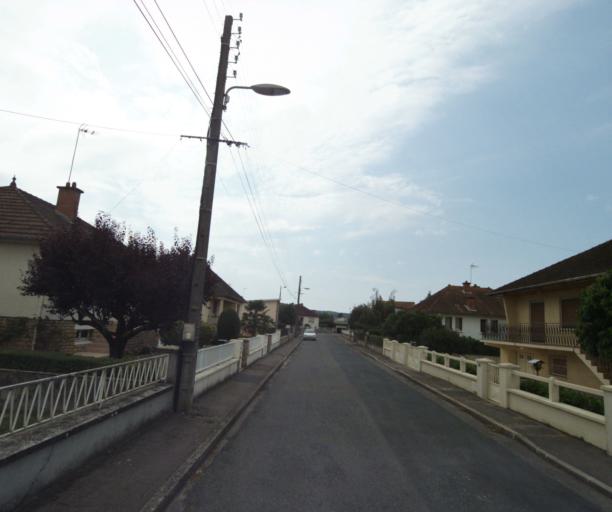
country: FR
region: Bourgogne
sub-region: Departement de Saone-et-Loire
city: Gueugnon
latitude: 46.6040
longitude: 4.0593
